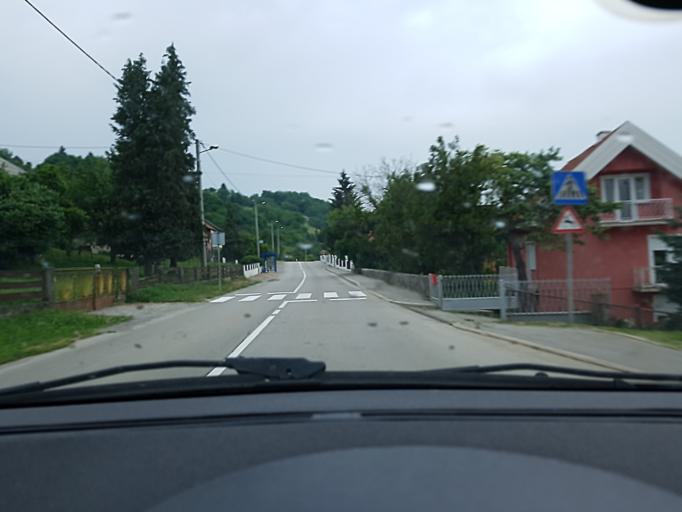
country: HR
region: Zagrebacka
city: Pojatno
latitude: 45.9181
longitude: 15.8077
